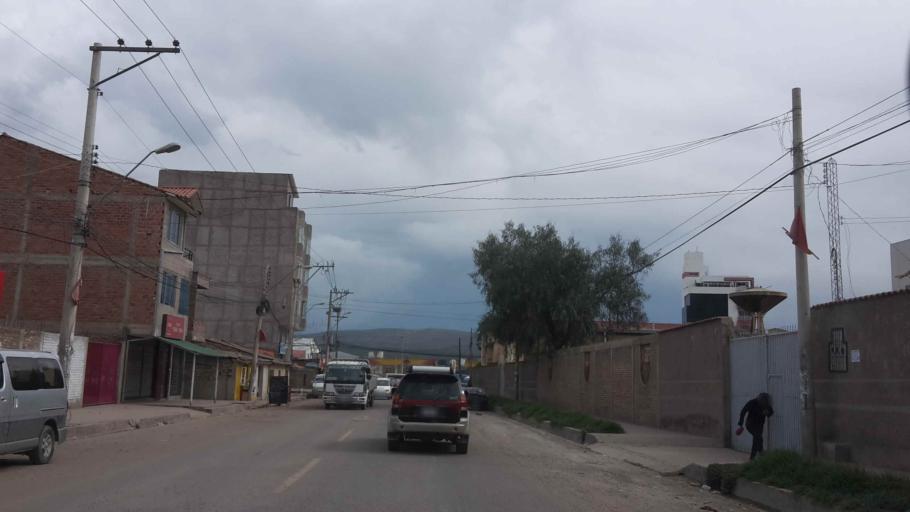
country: BO
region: Cochabamba
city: Cochabamba
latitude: -17.3899
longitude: -66.2507
